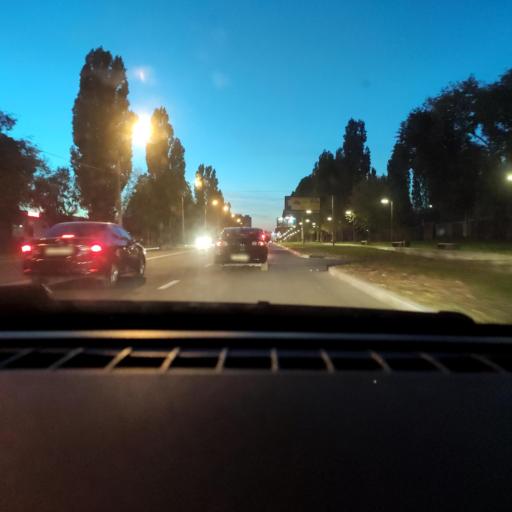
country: RU
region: Voronezj
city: Voronezh
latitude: 51.6681
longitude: 39.2626
